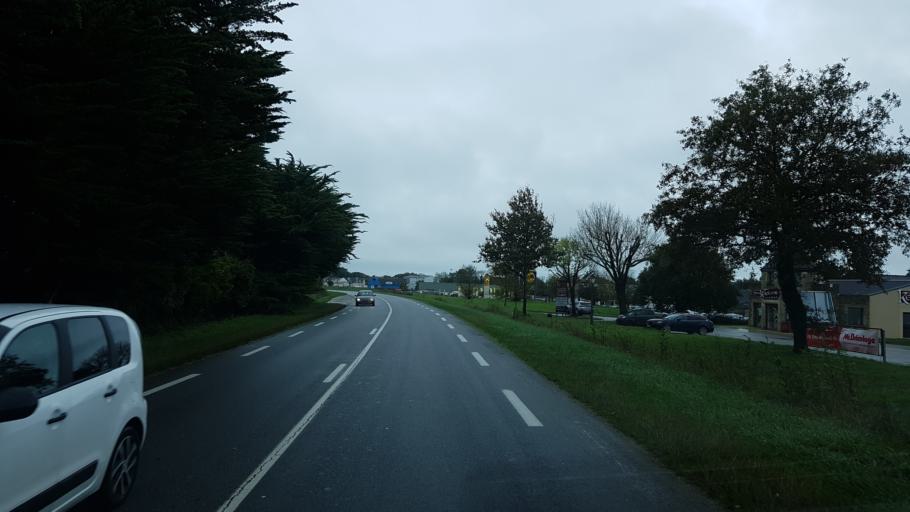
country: FR
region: Brittany
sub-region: Departement du Morbihan
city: Sarzeau
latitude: 47.5229
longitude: -2.7847
